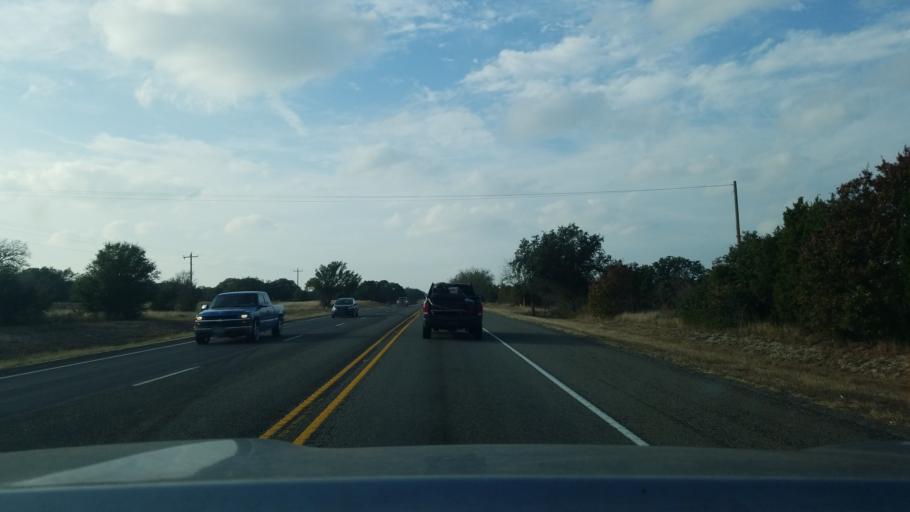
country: US
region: Texas
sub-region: Lampasas County
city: Lampasas
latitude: 31.1803
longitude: -98.3606
